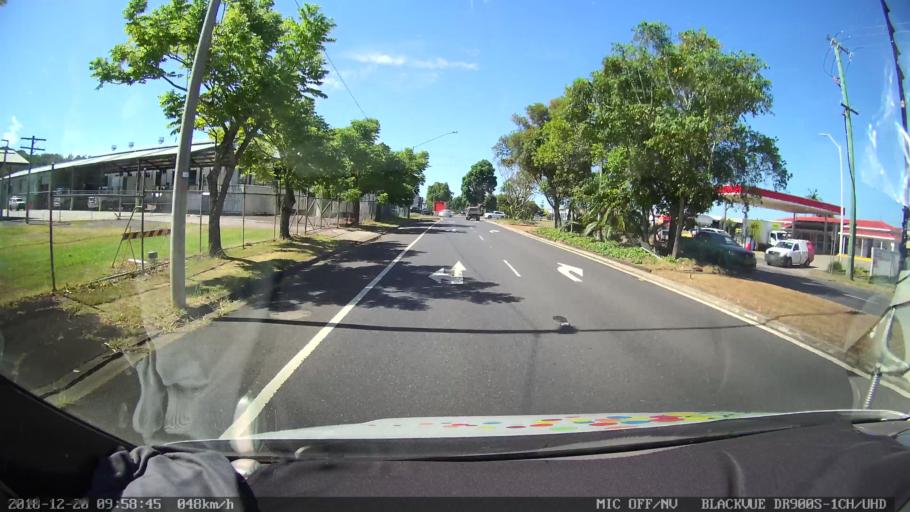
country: AU
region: New South Wales
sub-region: Lismore Municipality
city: Lismore
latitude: -28.8201
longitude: 153.2653
